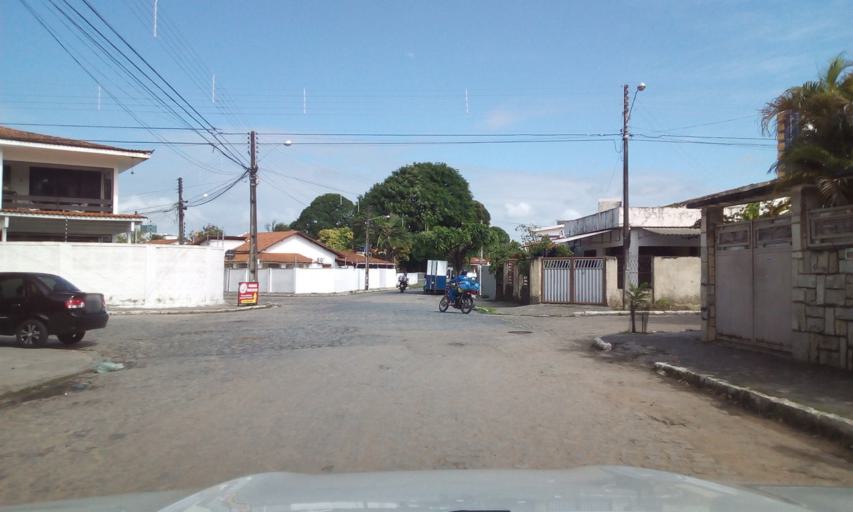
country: BR
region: Paraiba
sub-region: Joao Pessoa
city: Joao Pessoa
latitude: -7.1240
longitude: -34.8558
